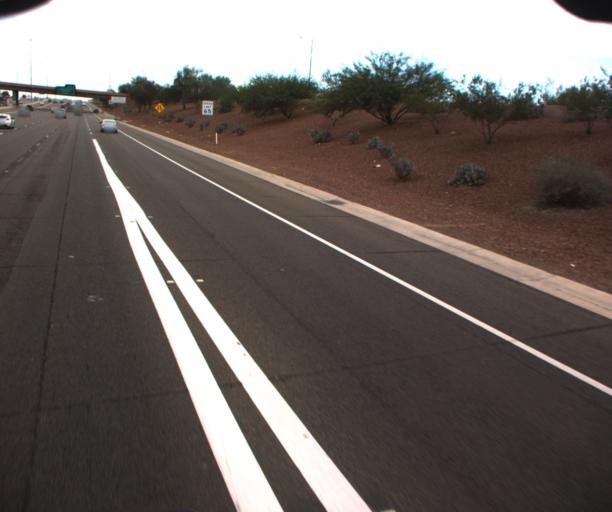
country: US
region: Arizona
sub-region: Maricopa County
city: Tempe Junction
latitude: 33.4361
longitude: -111.9523
